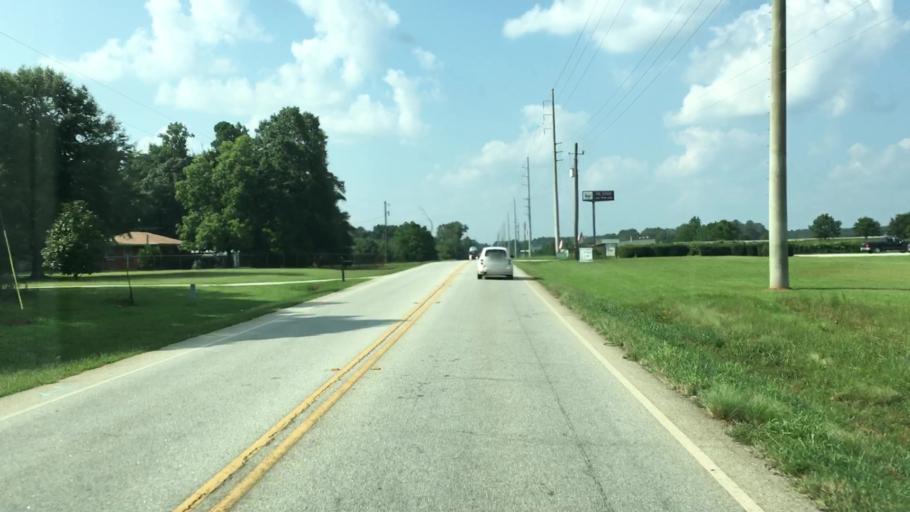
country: US
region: Georgia
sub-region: Walton County
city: Social Circle
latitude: 33.5926
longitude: -83.7487
